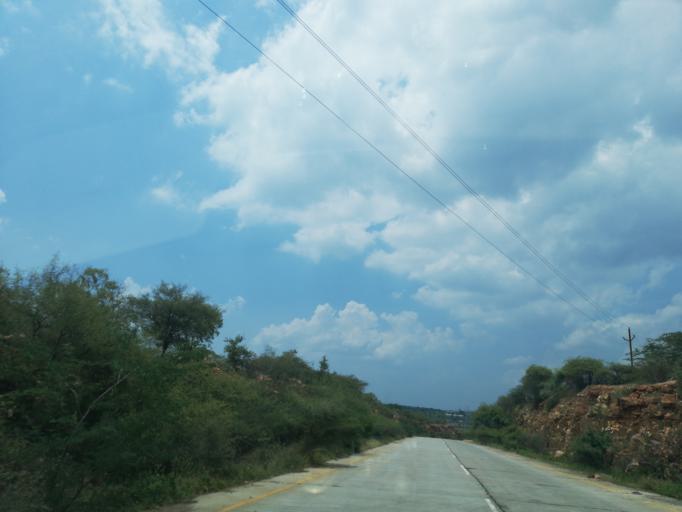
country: IN
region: Andhra Pradesh
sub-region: Guntur
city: Macherla
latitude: 16.5707
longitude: 79.3320
